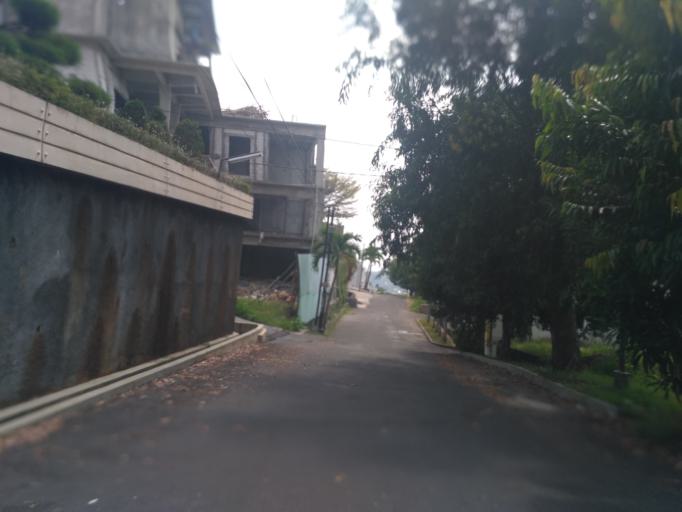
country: ID
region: Central Java
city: Semarang
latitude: -7.0415
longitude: 110.4286
